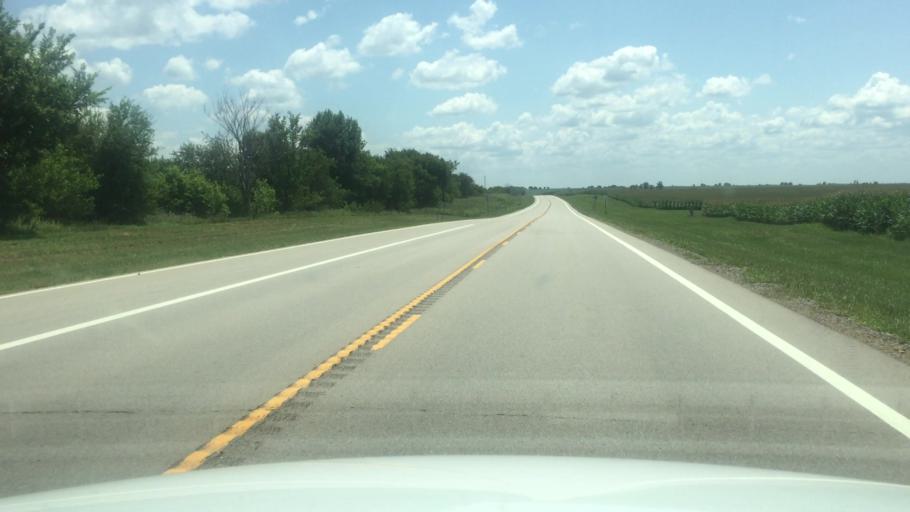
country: US
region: Kansas
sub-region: Brown County
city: Horton
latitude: 39.6370
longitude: -95.3541
